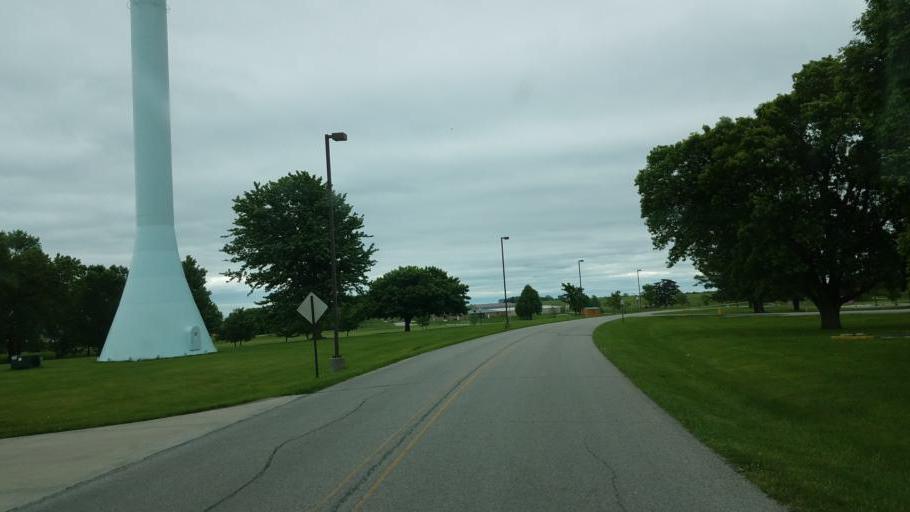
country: US
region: Iowa
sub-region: Decatur County
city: Lamoni
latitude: 40.6181
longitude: -93.9245
